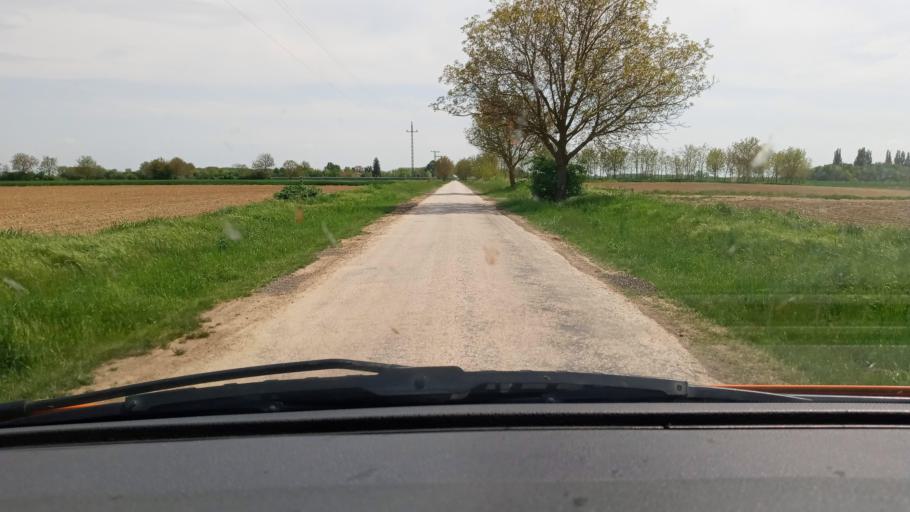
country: HU
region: Baranya
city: Villany
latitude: 45.8108
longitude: 18.5145
